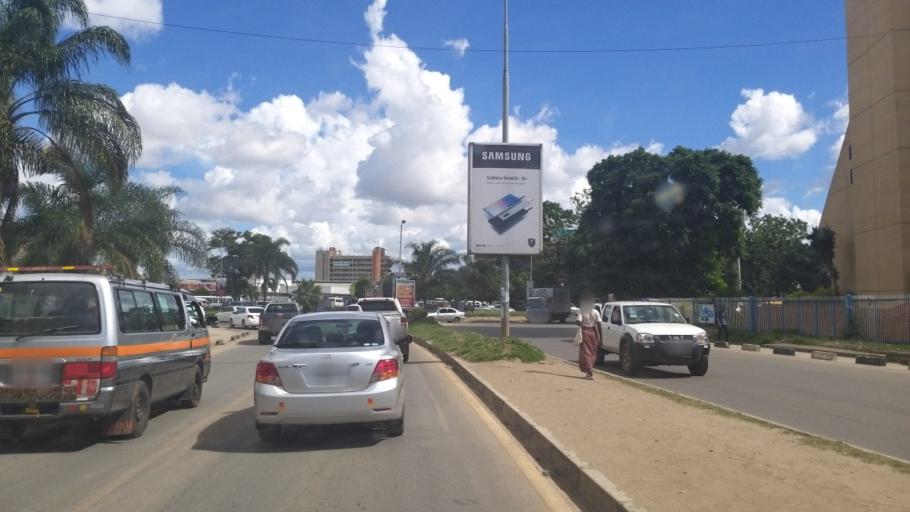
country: ZM
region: Lusaka
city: Lusaka
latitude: -15.4079
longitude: 28.2800
